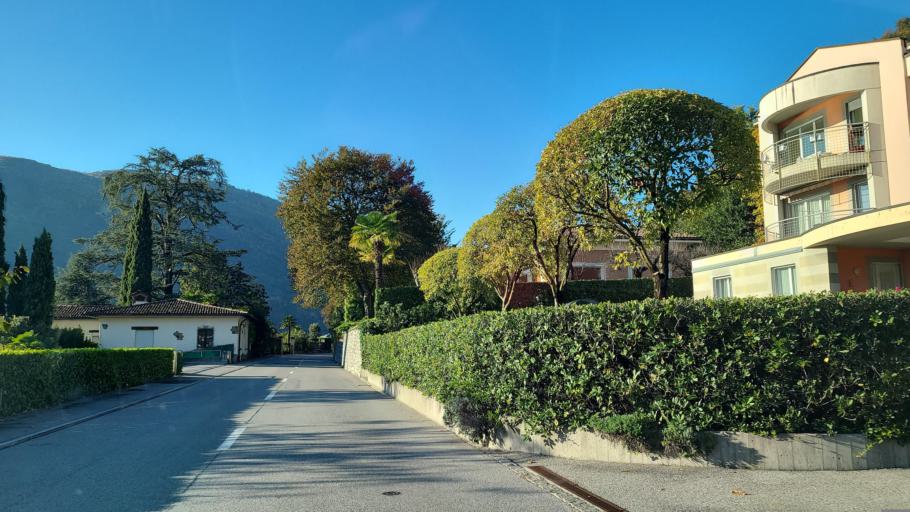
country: IT
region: Lombardy
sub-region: Provincia di Varese
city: Porto Ceresio
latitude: 45.9280
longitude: 8.9055
